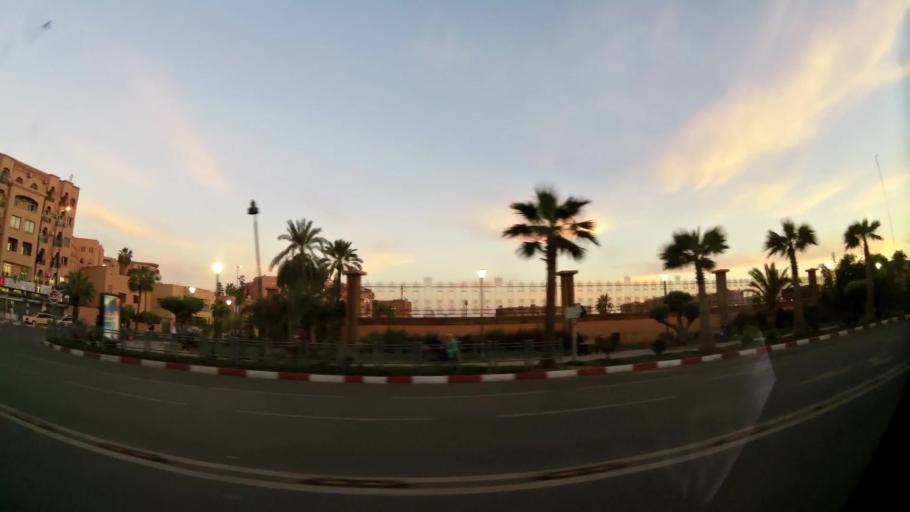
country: MA
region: Marrakech-Tensift-Al Haouz
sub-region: Marrakech
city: Marrakesh
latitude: 31.6405
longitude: -8.0005
